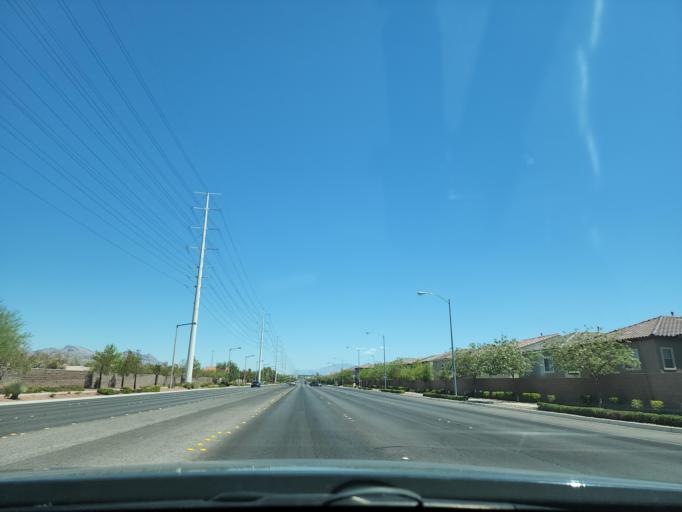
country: US
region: Nevada
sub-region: Clark County
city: Summerlin South
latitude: 36.0946
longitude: -115.3153
